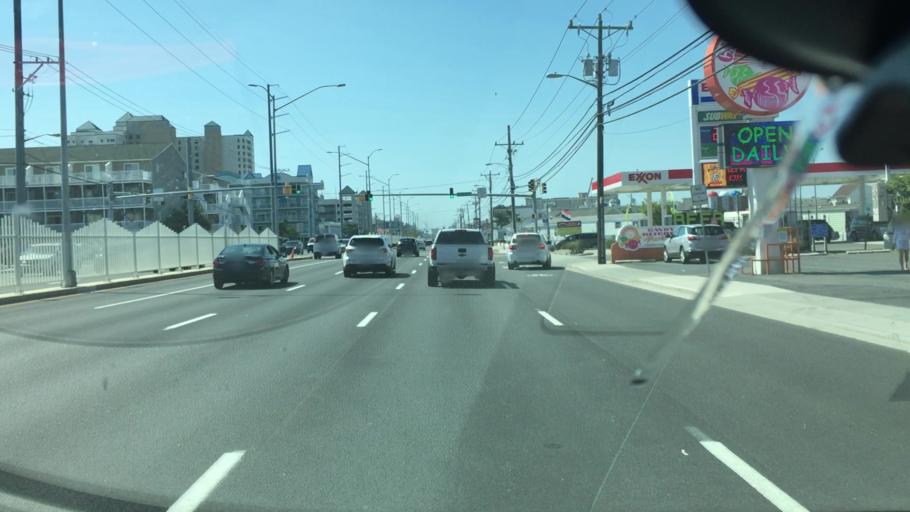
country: US
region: Maryland
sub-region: Worcester County
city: Ocean City
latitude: 38.3778
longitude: -75.0689
